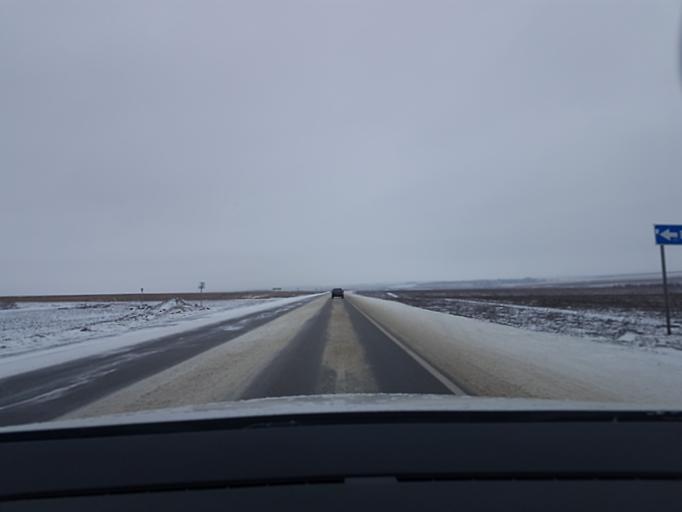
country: RU
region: Rjazan
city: Skopin
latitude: 53.9688
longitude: 39.4001
